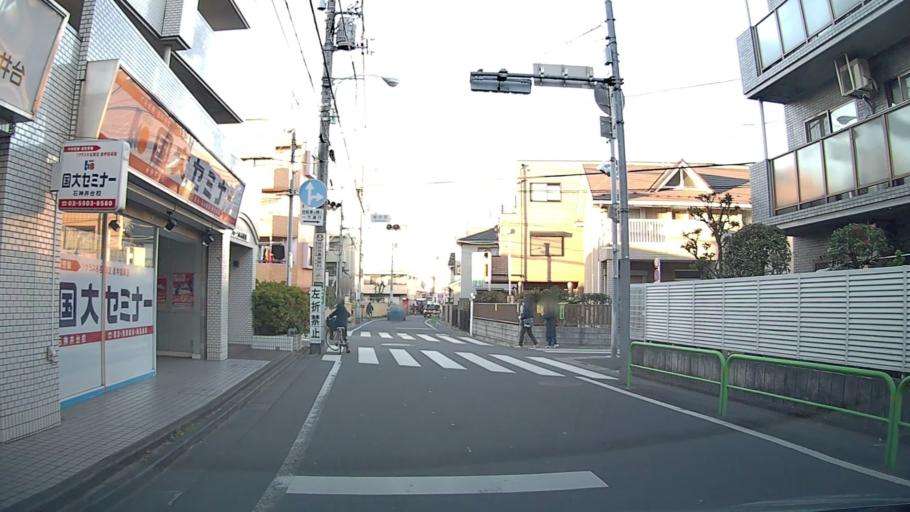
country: JP
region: Tokyo
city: Musashino
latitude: 35.7372
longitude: 139.5890
